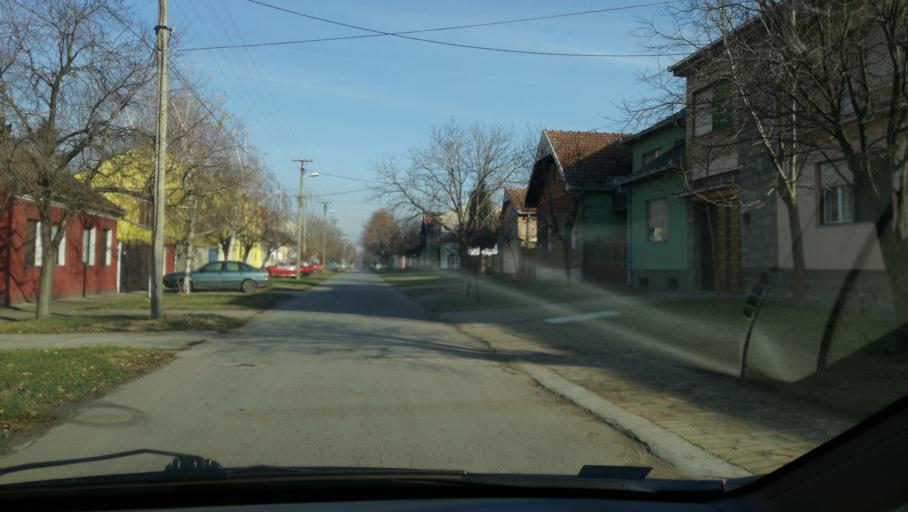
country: RS
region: Autonomna Pokrajina Vojvodina
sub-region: Severnobanatski Okrug
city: Kikinda
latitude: 45.8225
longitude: 20.4575
